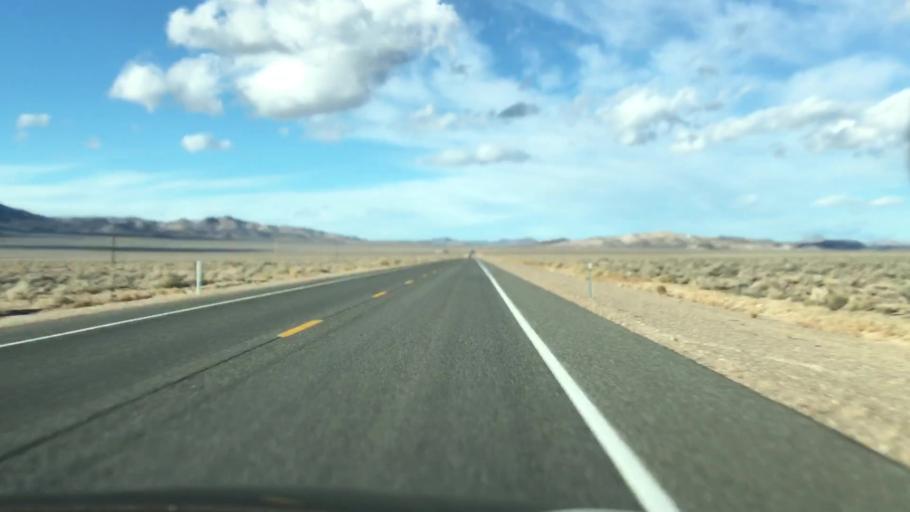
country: US
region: Nevada
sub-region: Esmeralda County
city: Goldfield
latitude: 37.4770
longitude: -117.1779
